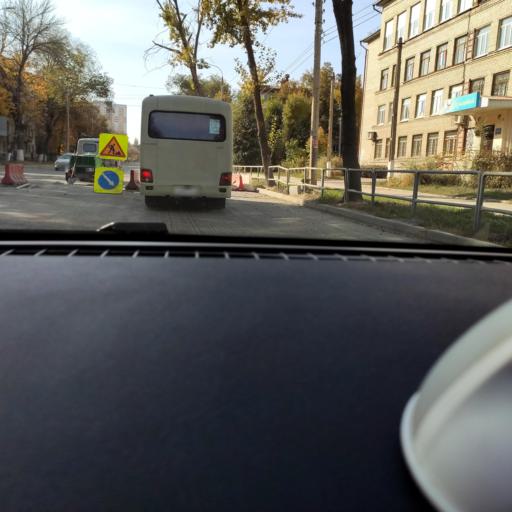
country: RU
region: Samara
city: Petra-Dubrava
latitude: 53.2206
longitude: 50.2703
